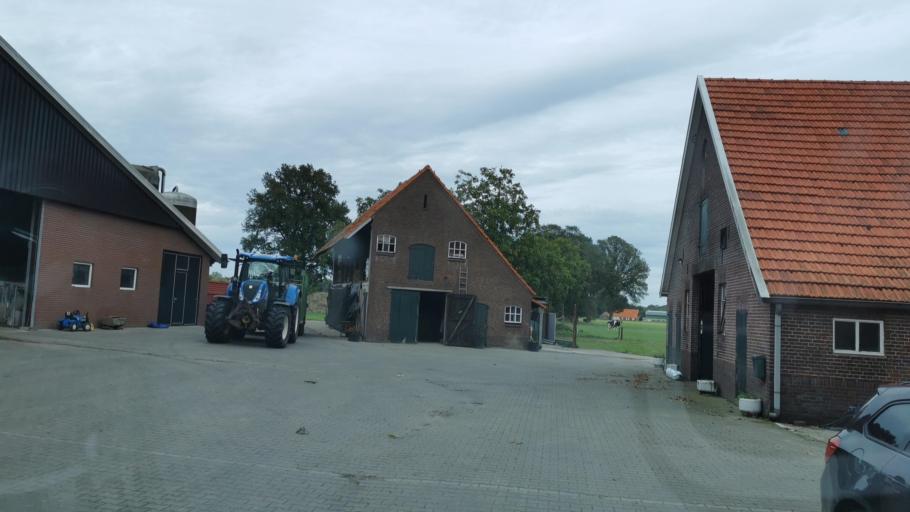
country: NL
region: Overijssel
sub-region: Gemeente Losser
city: Losser
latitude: 52.3152
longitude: 7.0186
